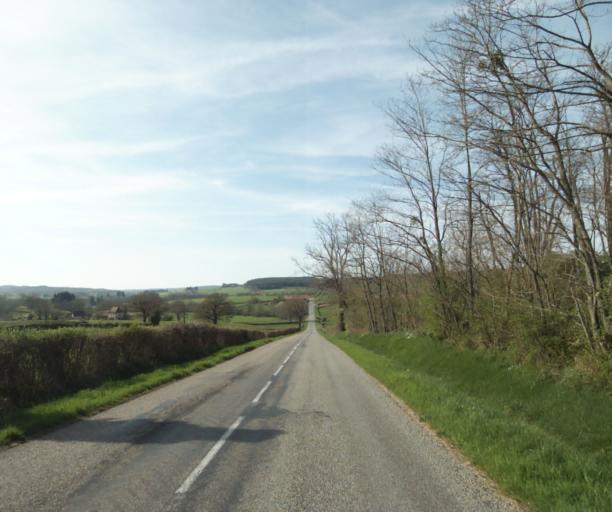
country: FR
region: Bourgogne
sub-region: Departement de Saone-et-Loire
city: Charolles
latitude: 46.4320
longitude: 4.4171
